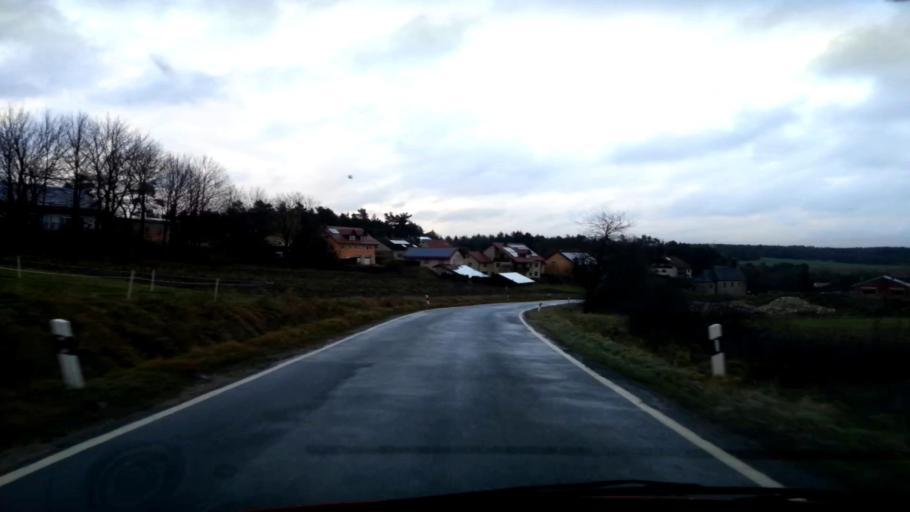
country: DE
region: Bavaria
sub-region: Upper Franconia
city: Poxdorf
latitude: 49.9224
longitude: 11.1215
